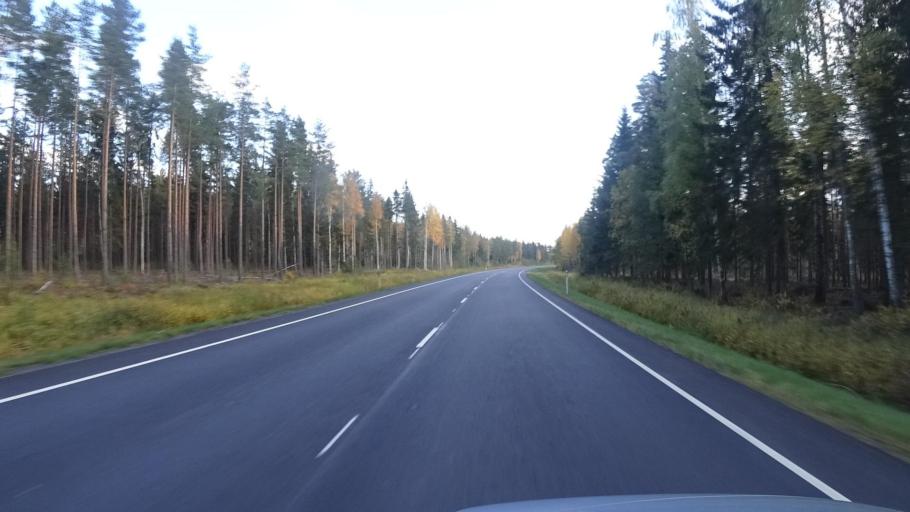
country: FI
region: Satakunta
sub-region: Rauma
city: Koeylioe
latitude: 61.1029
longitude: 22.2318
